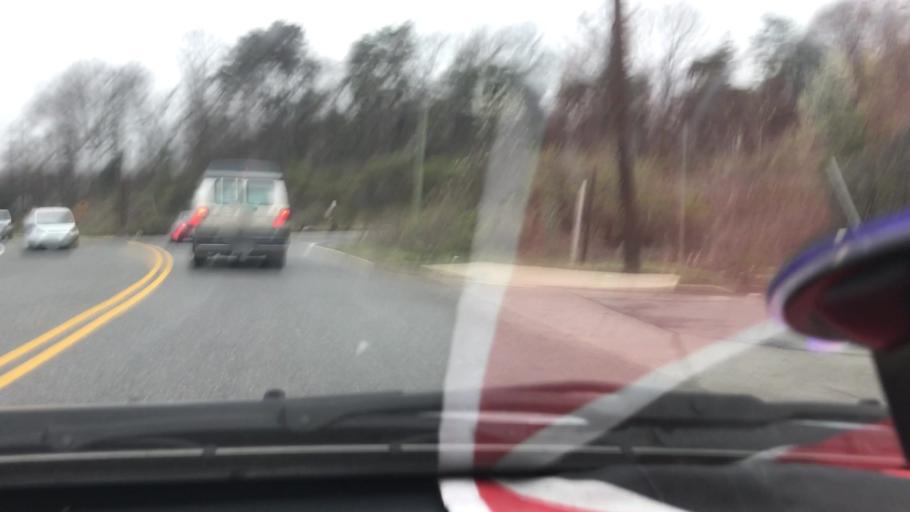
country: US
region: Maryland
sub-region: Prince George's County
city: Cheverly
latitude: 38.9152
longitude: -76.9055
